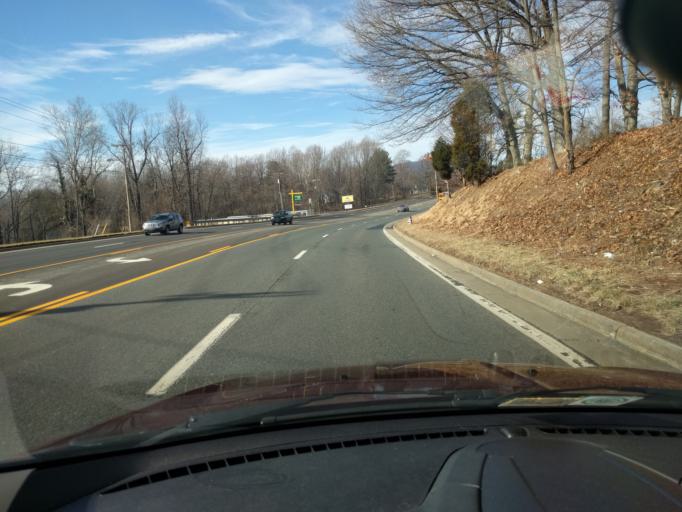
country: US
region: Virginia
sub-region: Amherst County
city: Madison Heights
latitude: 37.4865
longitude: -79.1214
